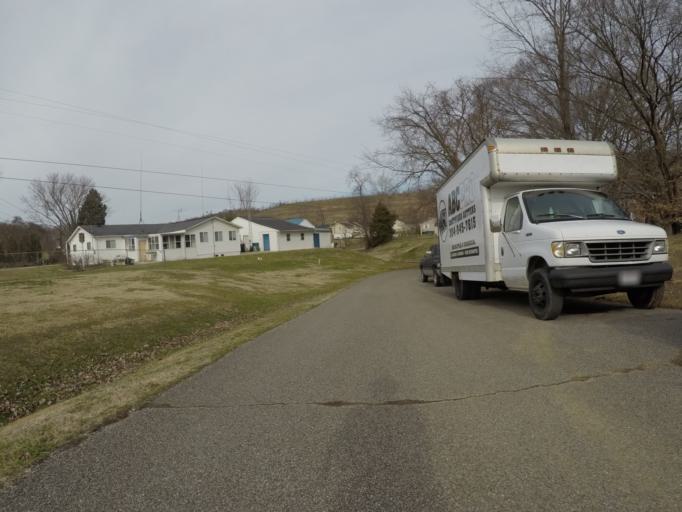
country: US
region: West Virginia
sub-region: Cabell County
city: Pea Ridge
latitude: 38.4466
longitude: -82.3717
